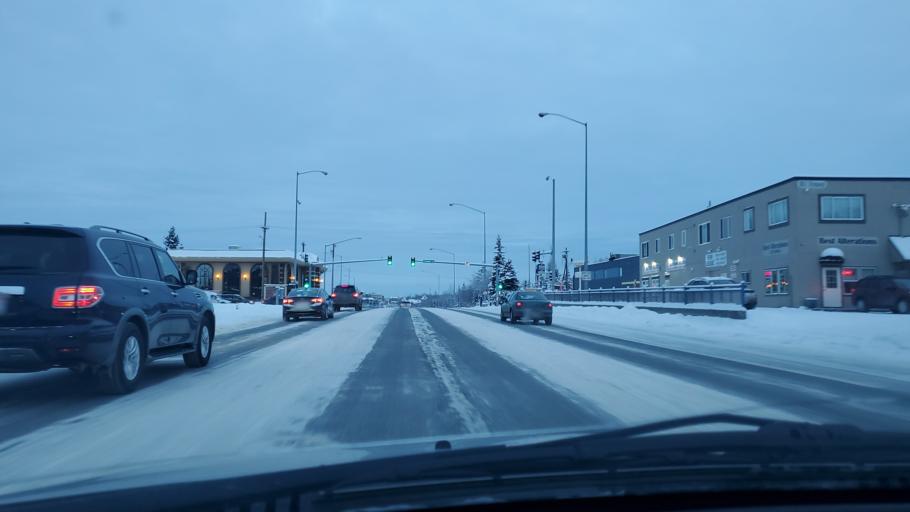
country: US
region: Alaska
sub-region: Anchorage Municipality
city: Anchorage
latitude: 61.1974
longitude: -149.8831
